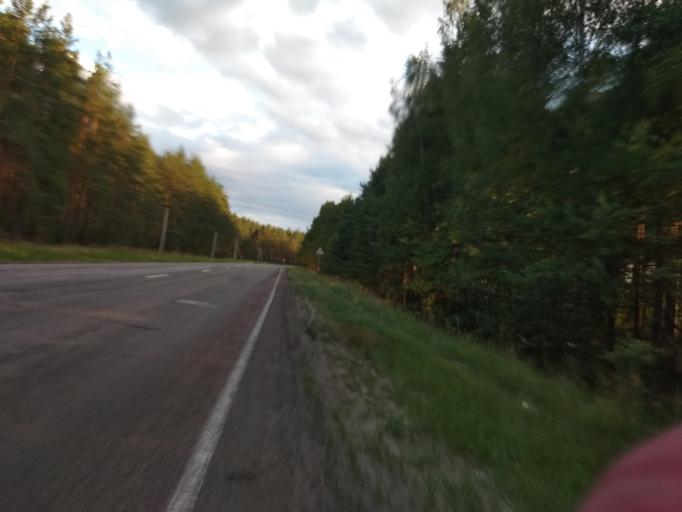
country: RU
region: Moskovskaya
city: Misheronskiy
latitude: 55.6291
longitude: 39.7413
